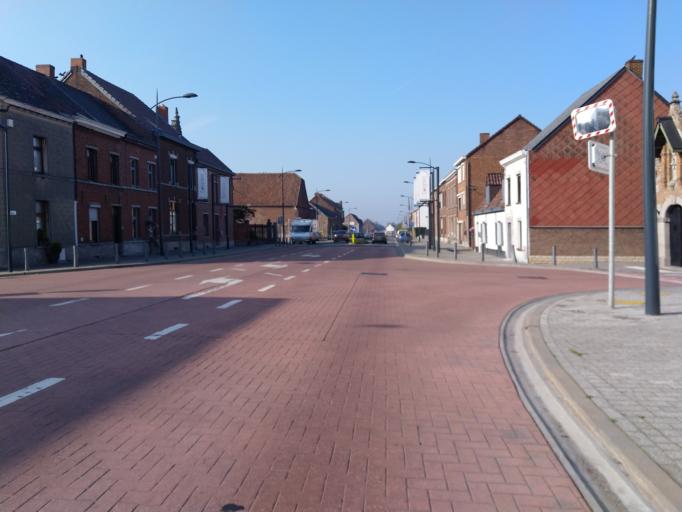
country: BE
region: Wallonia
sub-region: Province du Hainaut
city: Soignies
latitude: 50.5836
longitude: 4.0812
